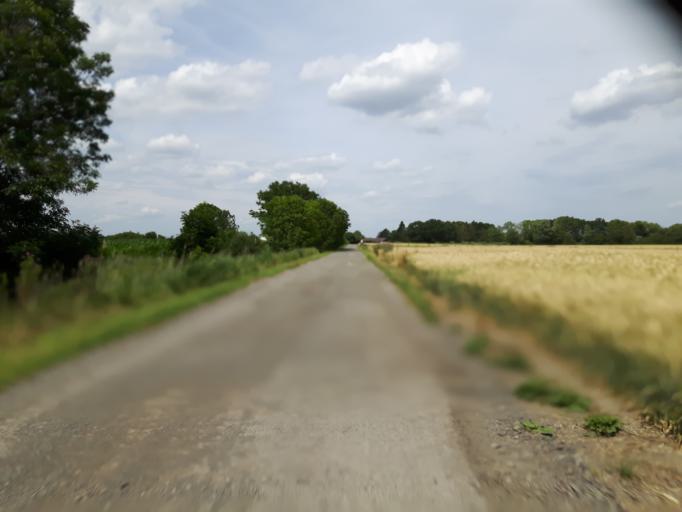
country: DE
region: Lower Saxony
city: Varel
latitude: 53.3988
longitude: 8.1863
